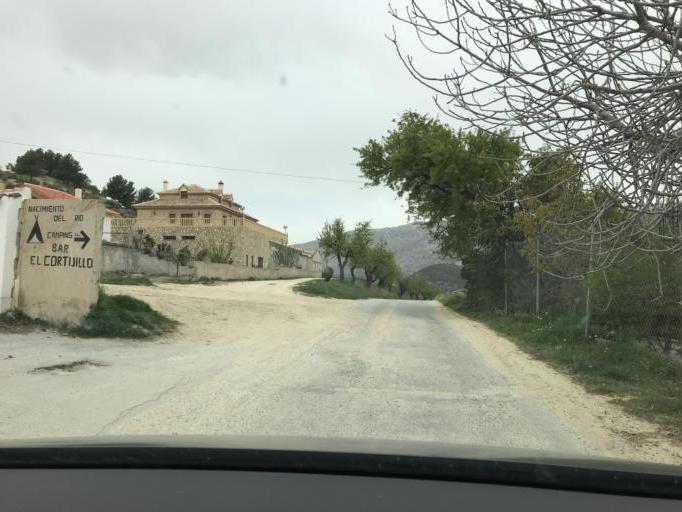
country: ES
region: Andalusia
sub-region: Provincia de Granada
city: Castril
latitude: 37.8166
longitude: -2.7633
